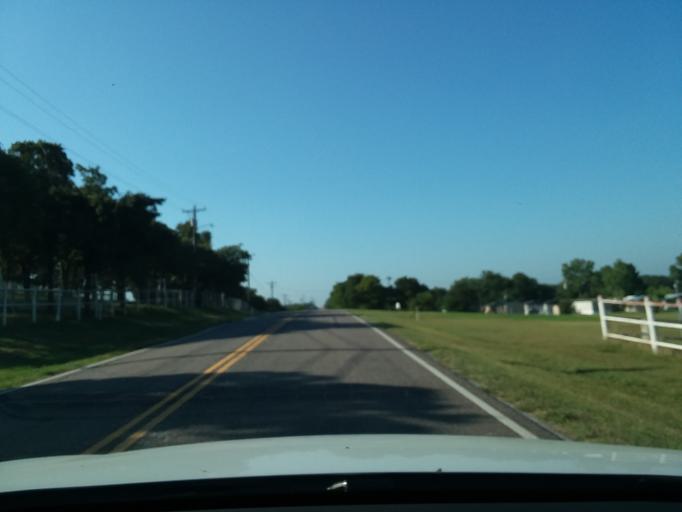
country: US
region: Texas
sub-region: Denton County
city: Bartonville
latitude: 33.0507
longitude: -97.1291
